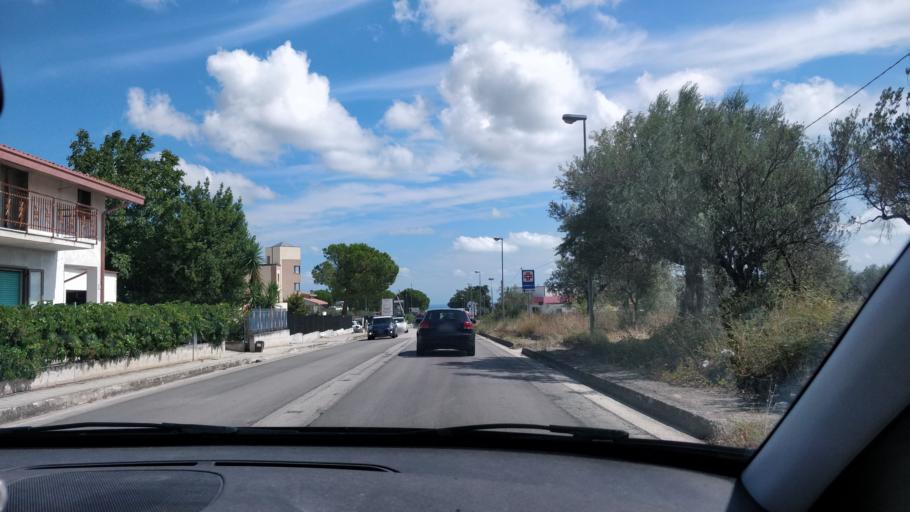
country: IT
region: Abruzzo
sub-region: Provincia di Chieti
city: Treglio
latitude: 42.2492
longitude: 14.4222
